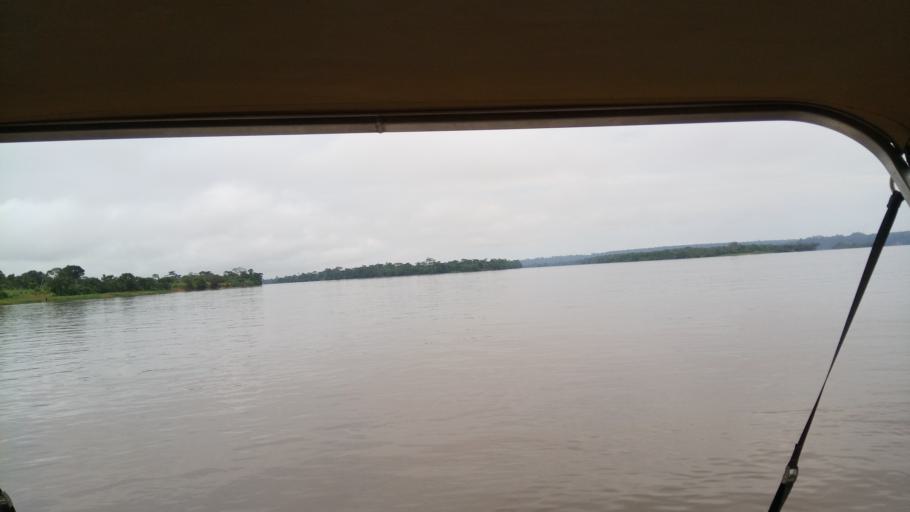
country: CD
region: Eastern Province
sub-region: Sous-Region de la Tshopo
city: Yangambi
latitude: 0.7152
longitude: 24.5613
